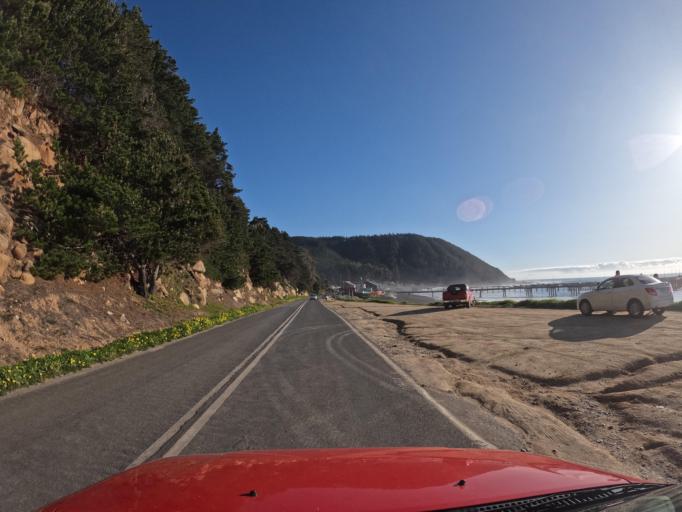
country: CL
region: Maule
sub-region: Provincia de Talca
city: Constitucion
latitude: -35.3562
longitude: -72.4526
